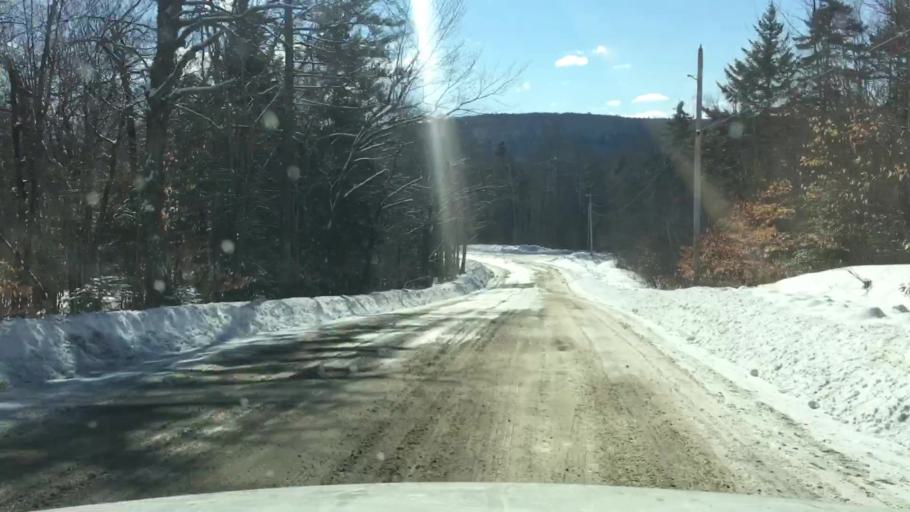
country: US
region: Maine
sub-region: Washington County
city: Calais
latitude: 45.0720
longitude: -67.4999
